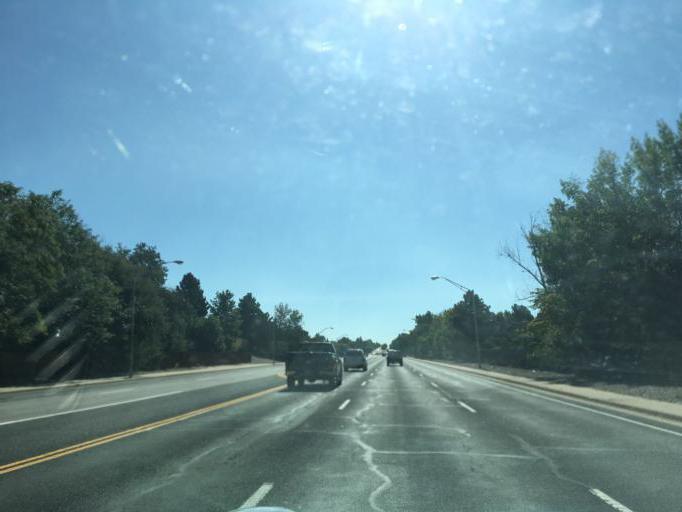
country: US
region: Colorado
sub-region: Arapahoe County
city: Dove Valley
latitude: 39.6345
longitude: -104.8159
